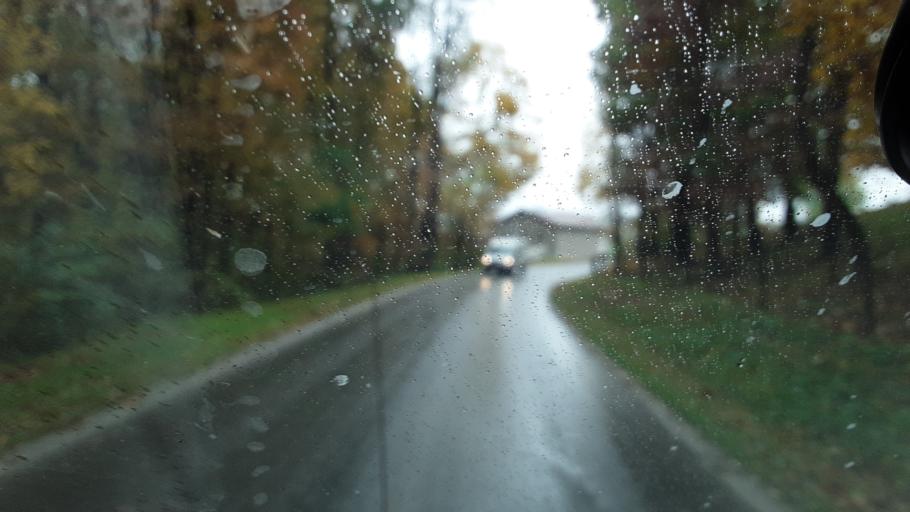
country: US
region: Ohio
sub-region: Tuscarawas County
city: Sugarcreek
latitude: 40.4395
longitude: -81.7675
